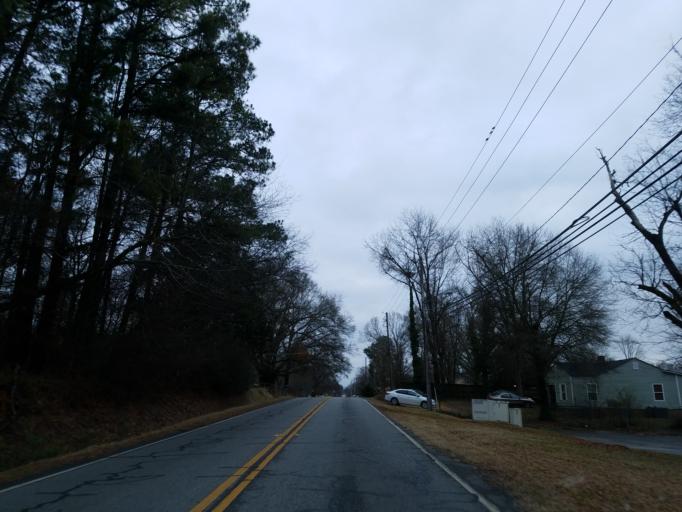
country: US
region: Georgia
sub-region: Bartow County
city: Cartersville
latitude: 34.2081
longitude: -84.8324
